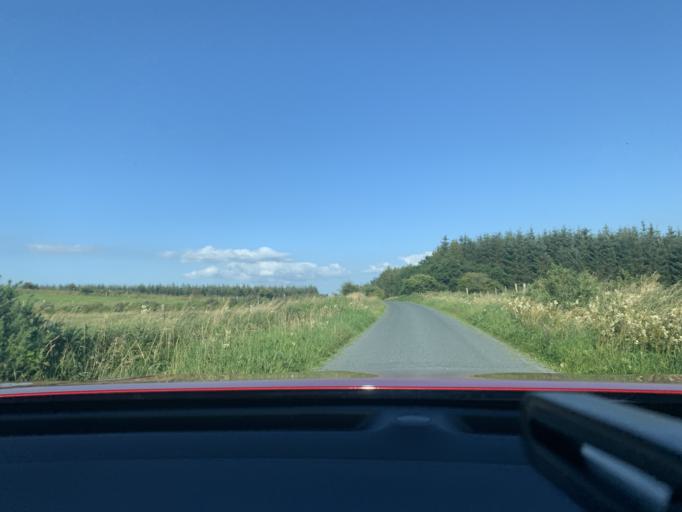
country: IE
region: Connaught
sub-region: Sligo
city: Tobercurry
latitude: 54.1519
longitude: -8.6681
